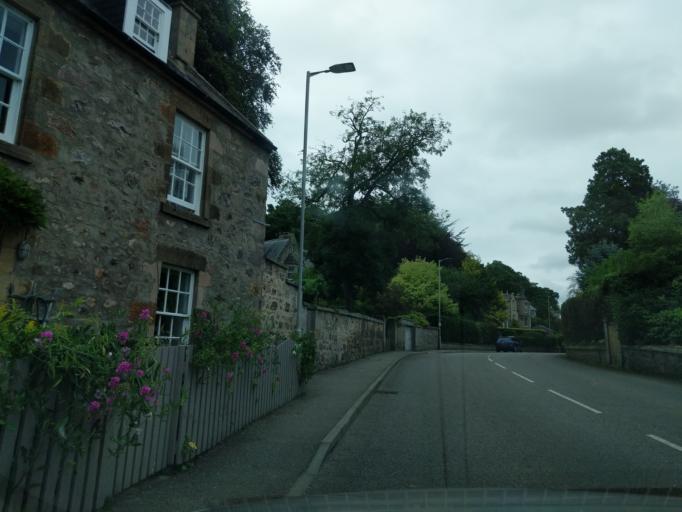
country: GB
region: Scotland
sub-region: Moray
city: Forres
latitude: 57.6086
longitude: -3.6078
